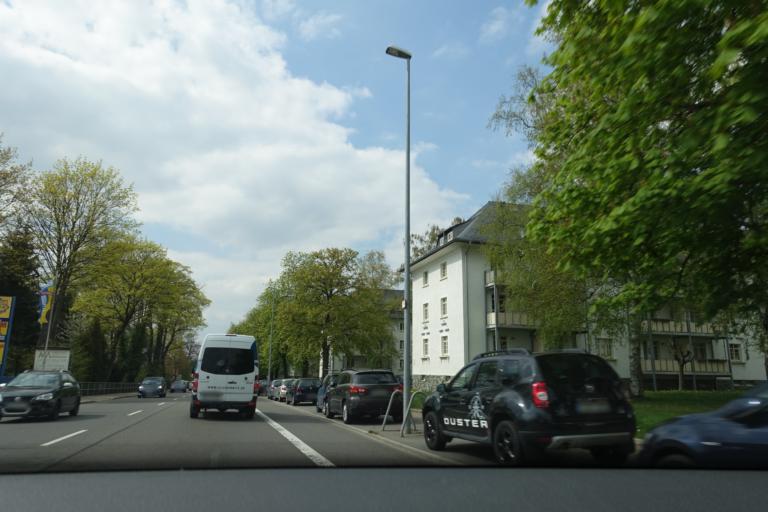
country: DE
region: Saxony
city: Chemnitz
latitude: 50.8171
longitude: 12.9486
